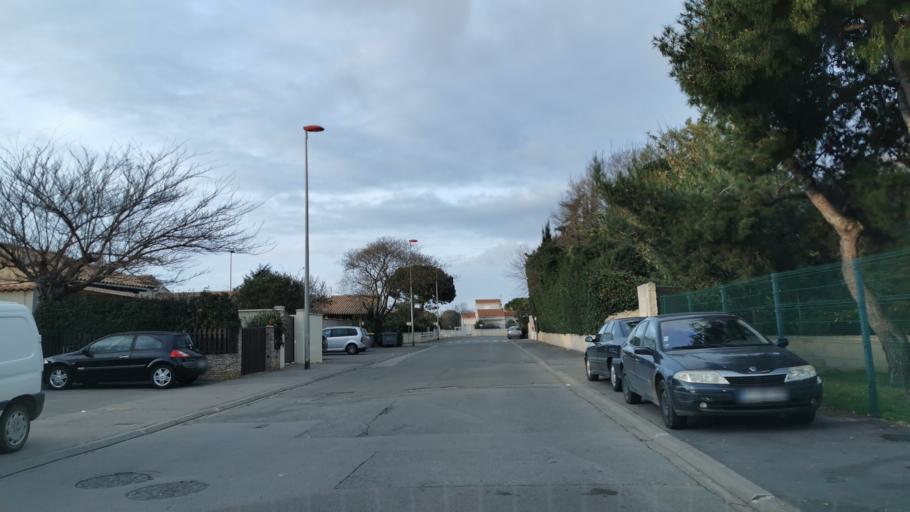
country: FR
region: Languedoc-Roussillon
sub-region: Departement de l'Aude
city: Narbonne
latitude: 43.1864
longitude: 2.9794
